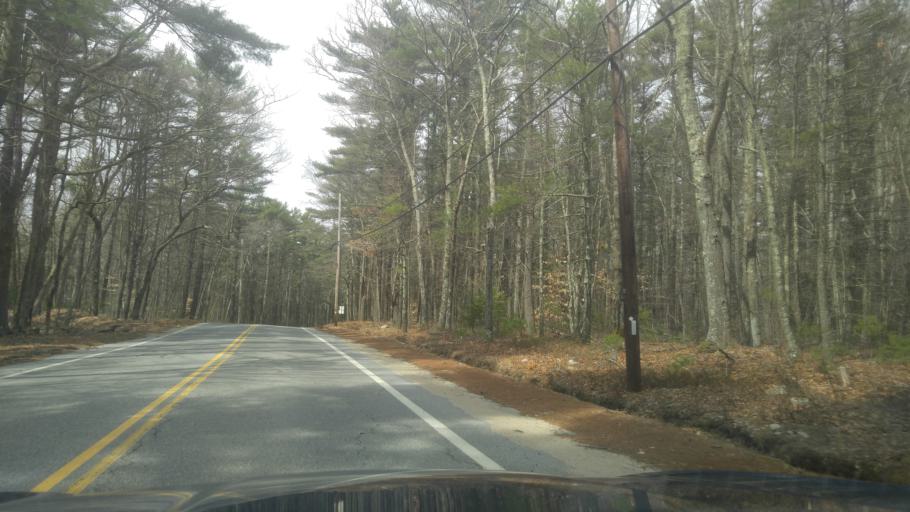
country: US
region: Rhode Island
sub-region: Washington County
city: Exeter
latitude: 41.6319
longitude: -71.5722
